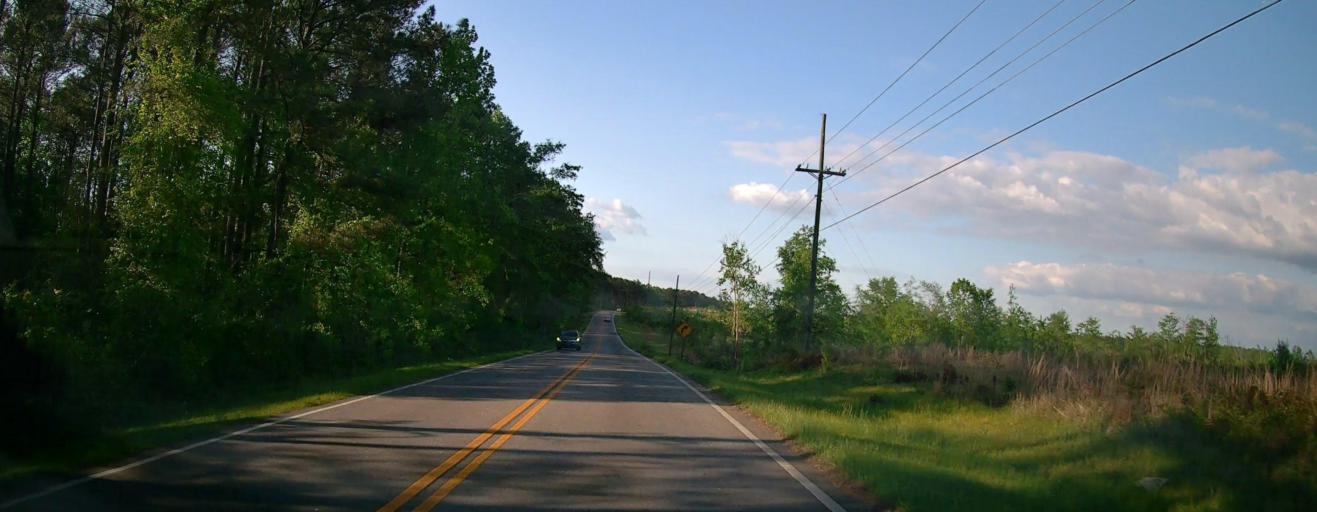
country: US
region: Georgia
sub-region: Putnam County
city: Eatonton
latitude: 33.2471
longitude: -83.3035
